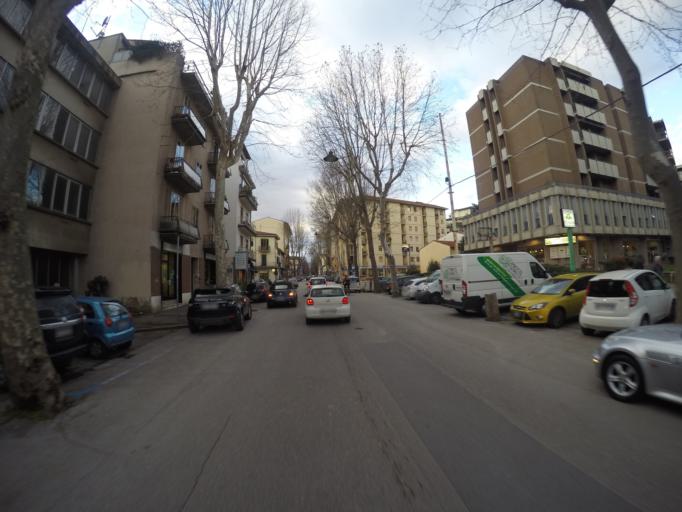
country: IT
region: Tuscany
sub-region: Provincia di Prato
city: Prato
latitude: 43.8717
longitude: 11.1096
